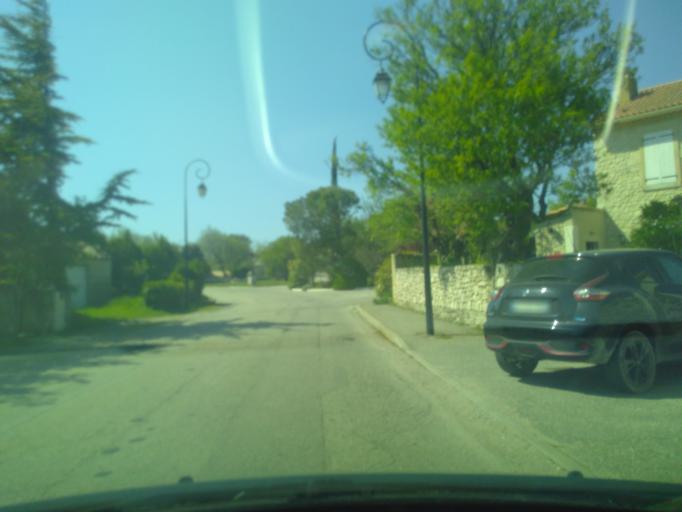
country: FR
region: Rhone-Alpes
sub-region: Departement de la Drome
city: Grignan
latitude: 44.4512
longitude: 4.9334
